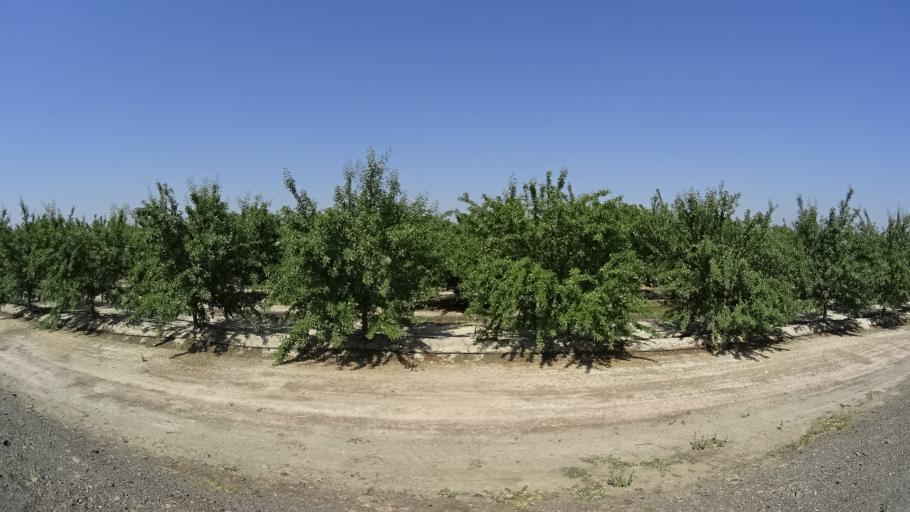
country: US
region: California
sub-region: Fresno County
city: Kingsburg
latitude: 36.4375
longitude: -119.5286
